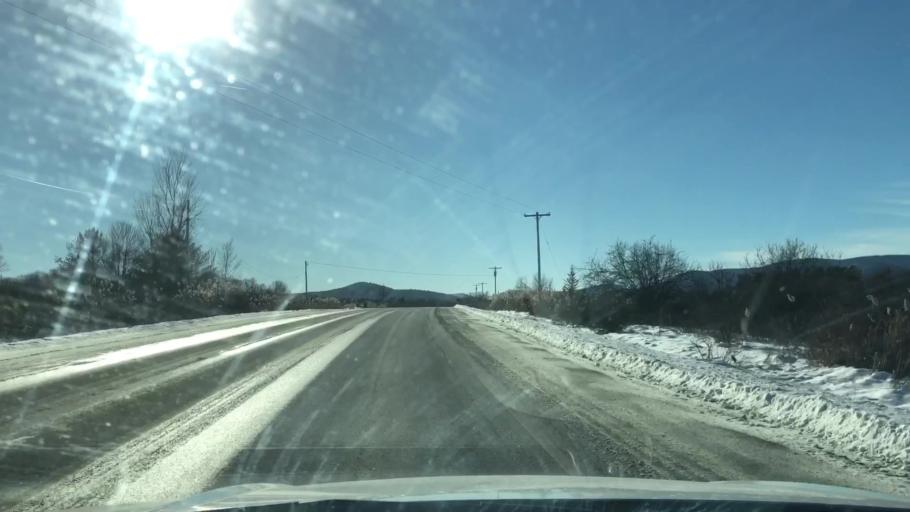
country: US
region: New York
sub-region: Essex County
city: Ticonderoga
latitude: 43.8672
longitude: -73.4055
